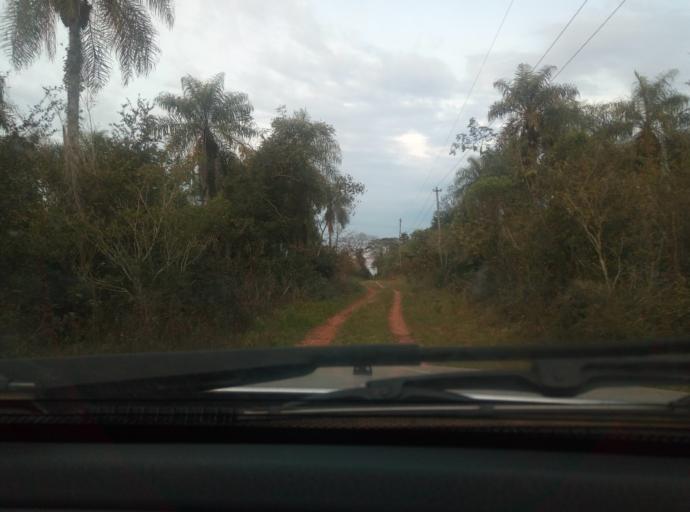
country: PY
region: Caaguazu
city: Carayao
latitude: -25.1473
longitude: -56.3906
